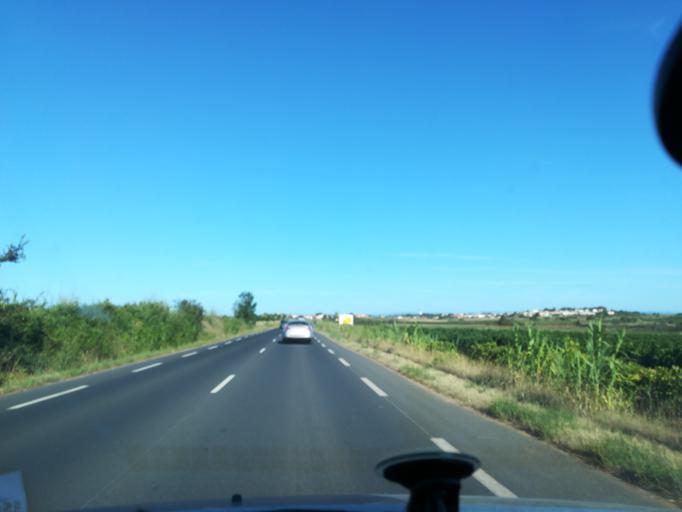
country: FR
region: Languedoc-Roussillon
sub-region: Departement de l'Herault
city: Portiragnes
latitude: 43.2947
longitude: 3.3562
